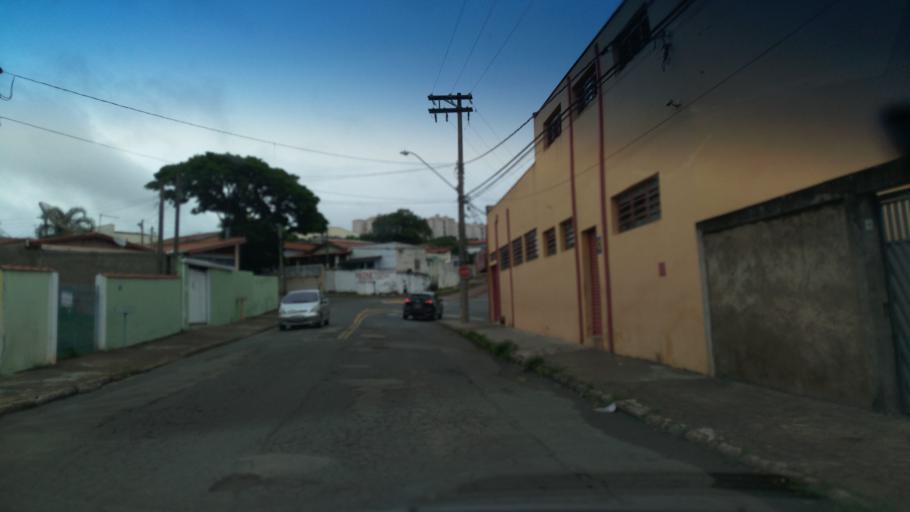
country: BR
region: Sao Paulo
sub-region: Valinhos
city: Valinhos
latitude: -22.9561
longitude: -47.0057
